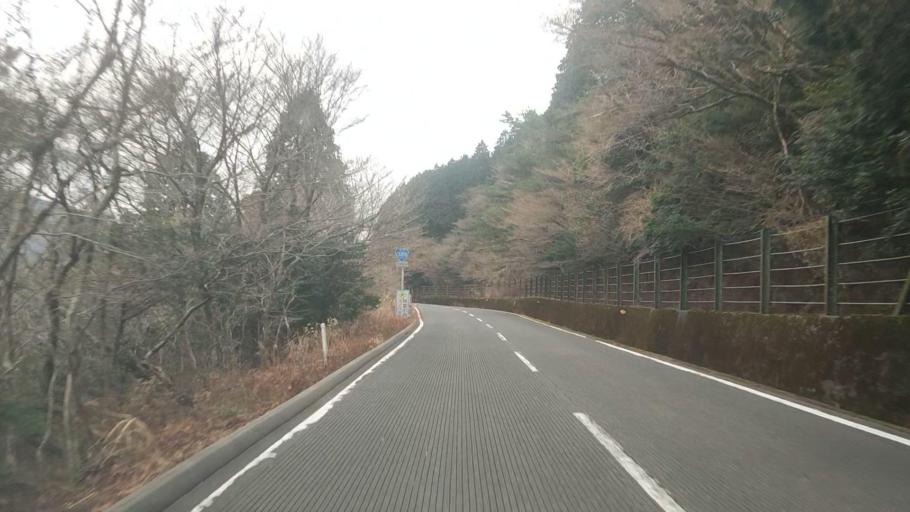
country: JP
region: Nagasaki
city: Shimabara
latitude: 32.7692
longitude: 130.2718
